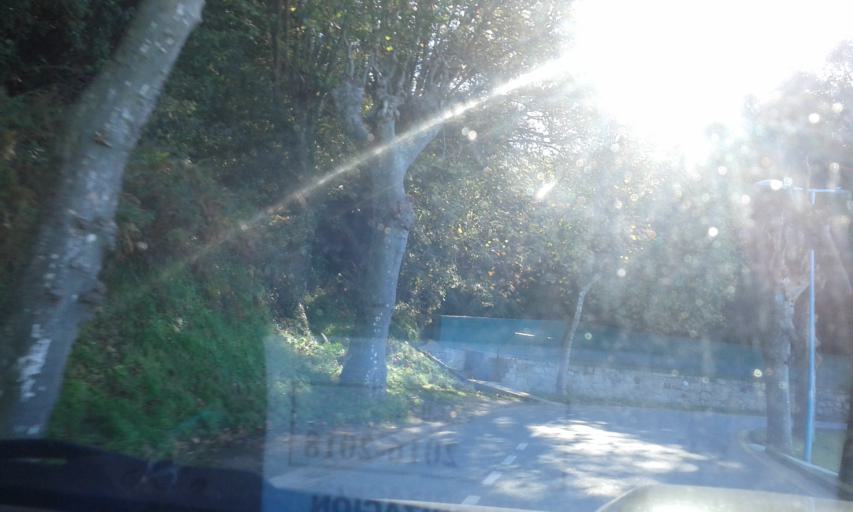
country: ES
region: Galicia
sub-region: Provincia de Pontevedra
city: Marin
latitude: 42.3909
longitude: -8.7142
